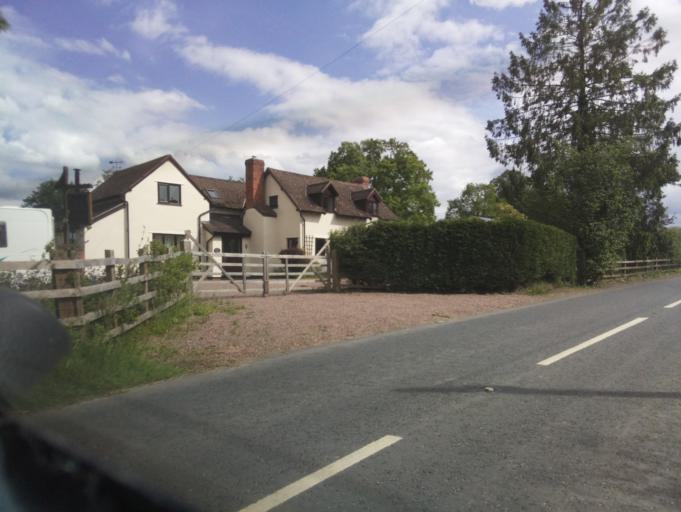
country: GB
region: England
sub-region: Herefordshire
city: Evesbatch
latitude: 52.1039
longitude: -2.4144
